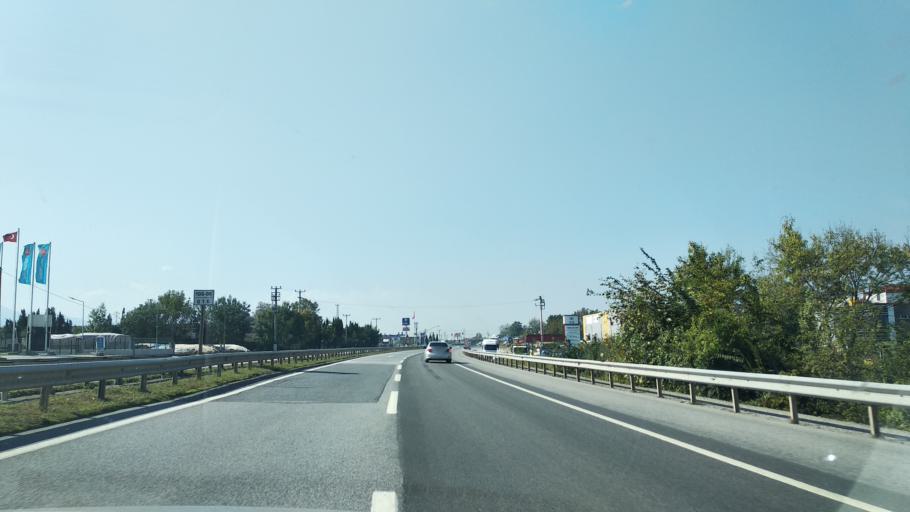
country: TR
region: Kocaeli
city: Derbent
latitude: 40.7295
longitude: 30.1474
